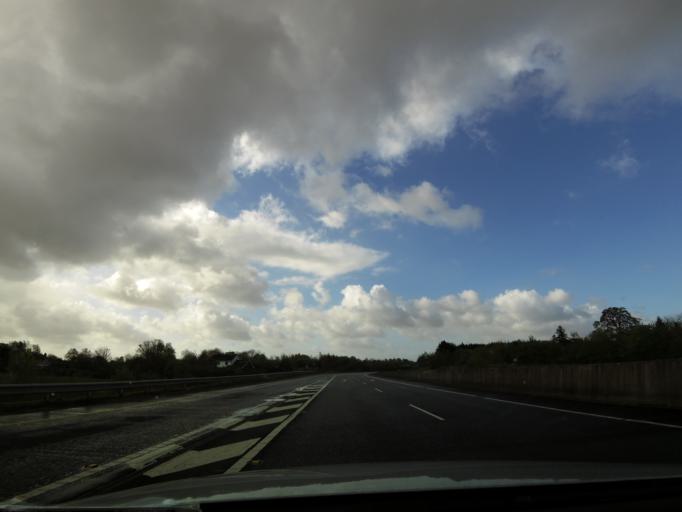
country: IE
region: Munster
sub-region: County Limerick
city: Annacotty
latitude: 52.6708
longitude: -8.5155
